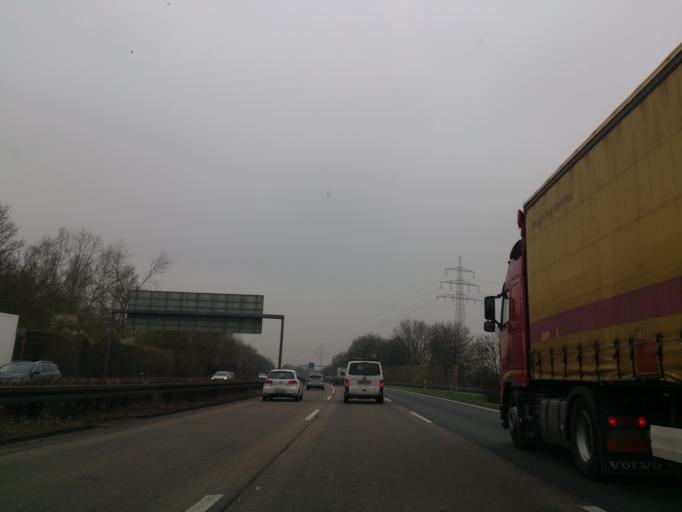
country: DE
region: North Rhine-Westphalia
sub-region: Regierungsbezirk Dusseldorf
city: Neuss
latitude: 51.1713
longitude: 6.7291
